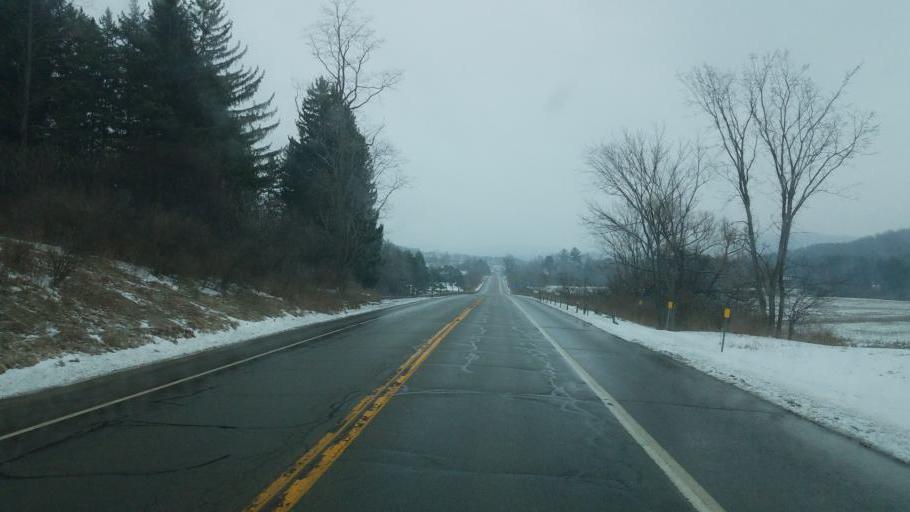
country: US
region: Pennsylvania
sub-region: Tioga County
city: Elkland
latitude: 42.0929
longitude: -77.4227
